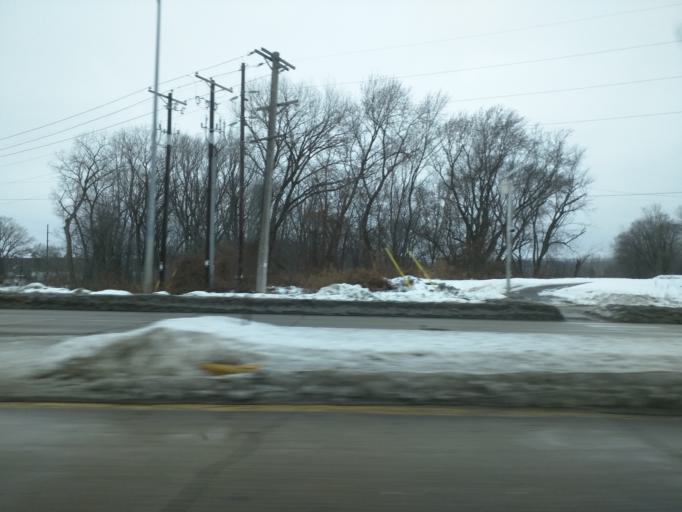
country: US
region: Wisconsin
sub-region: La Crosse County
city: La Crosse
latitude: 43.8203
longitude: -91.2491
